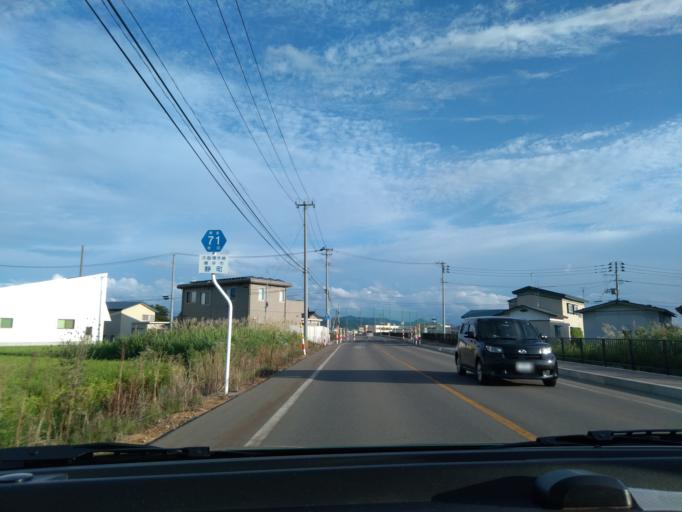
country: JP
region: Akita
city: Yokotemachi
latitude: 39.3322
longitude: 140.5447
